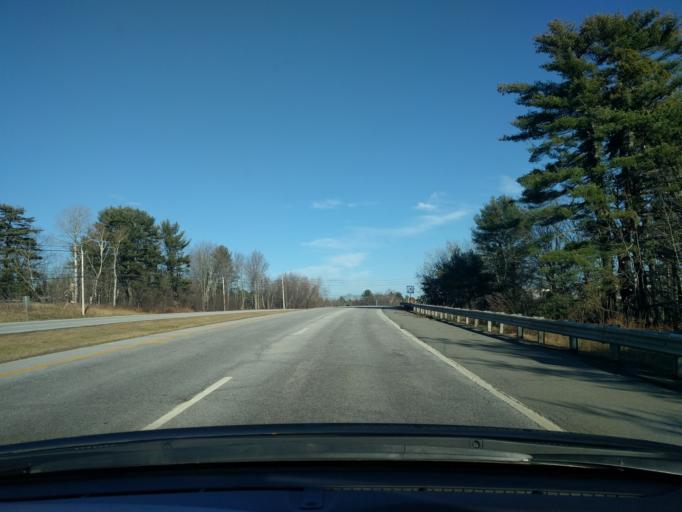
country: US
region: Maine
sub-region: Penobscot County
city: Hampden
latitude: 44.7521
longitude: -68.8429
